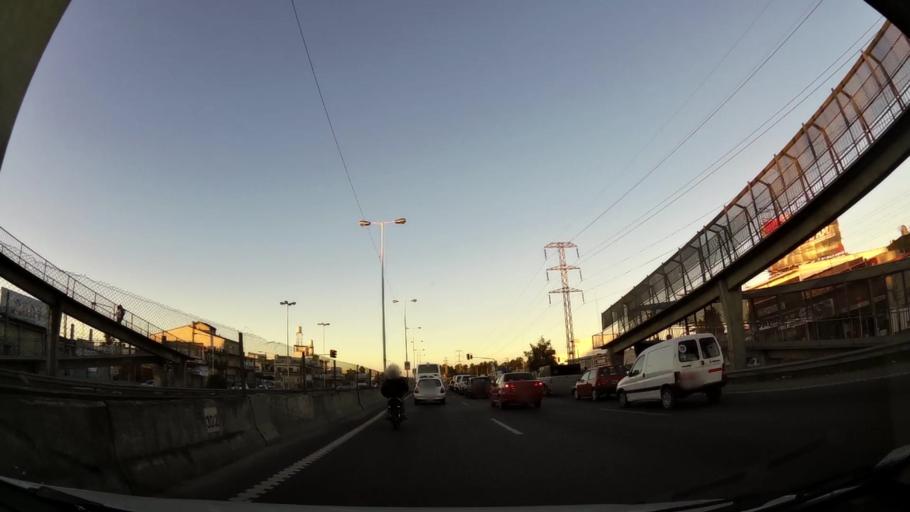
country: AR
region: Buenos Aires
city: Pontevedra
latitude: -34.7701
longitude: -58.6196
